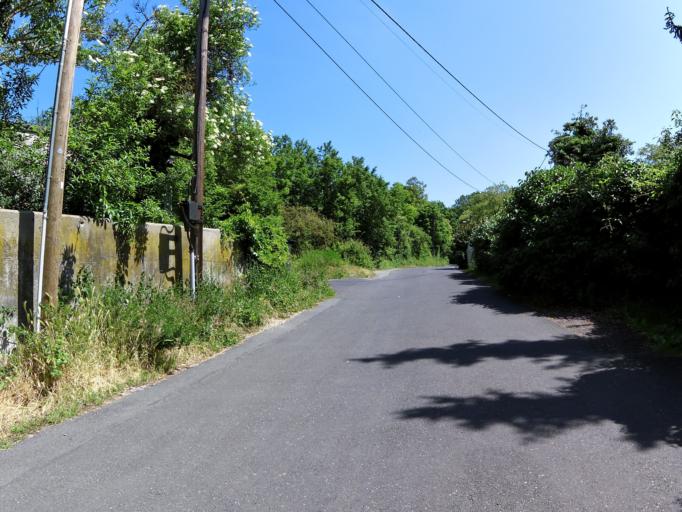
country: DE
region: Bavaria
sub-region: Regierungsbezirk Unterfranken
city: Wuerzburg
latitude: 49.7734
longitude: 9.9511
